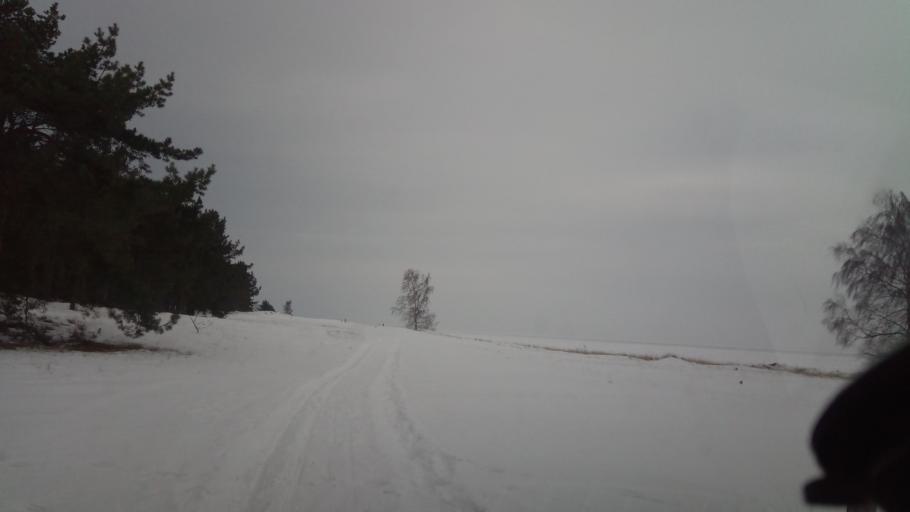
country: LT
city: Neringa
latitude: 55.4224
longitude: 21.1079
